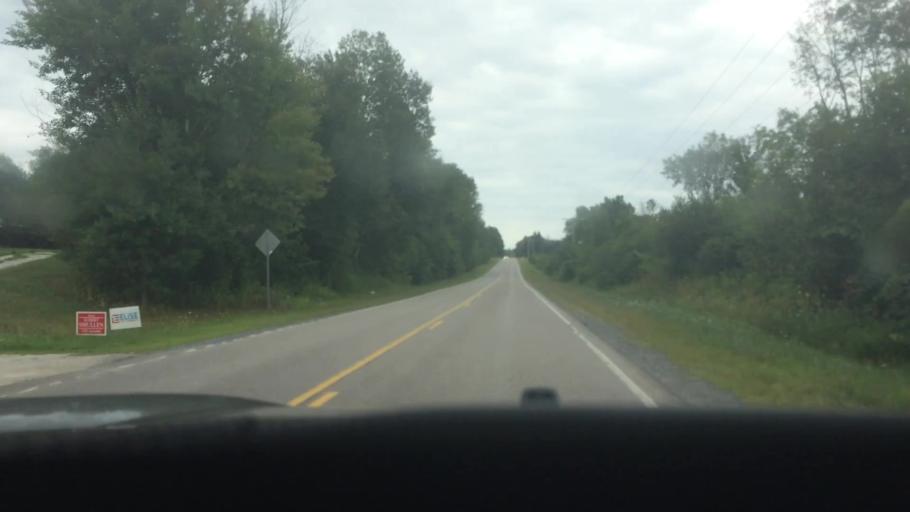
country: US
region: New York
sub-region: St. Lawrence County
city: Hannawa Falls
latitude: 44.5382
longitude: -75.0597
